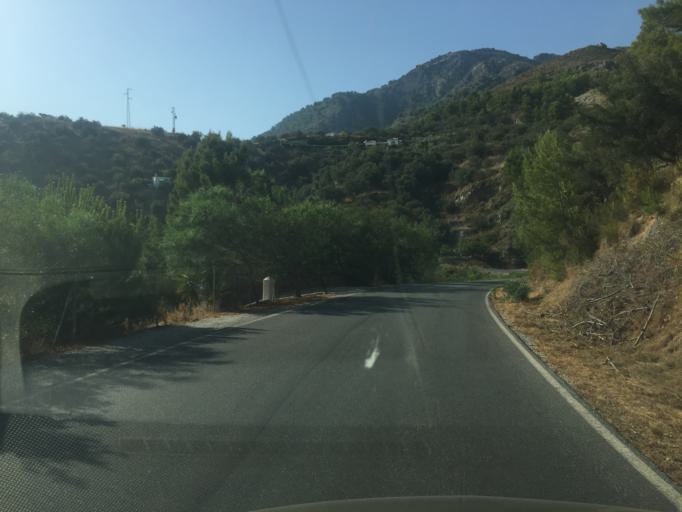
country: ES
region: Andalusia
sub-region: Provincia de Malaga
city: Frigiliana
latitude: 36.8011
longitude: -3.9085
